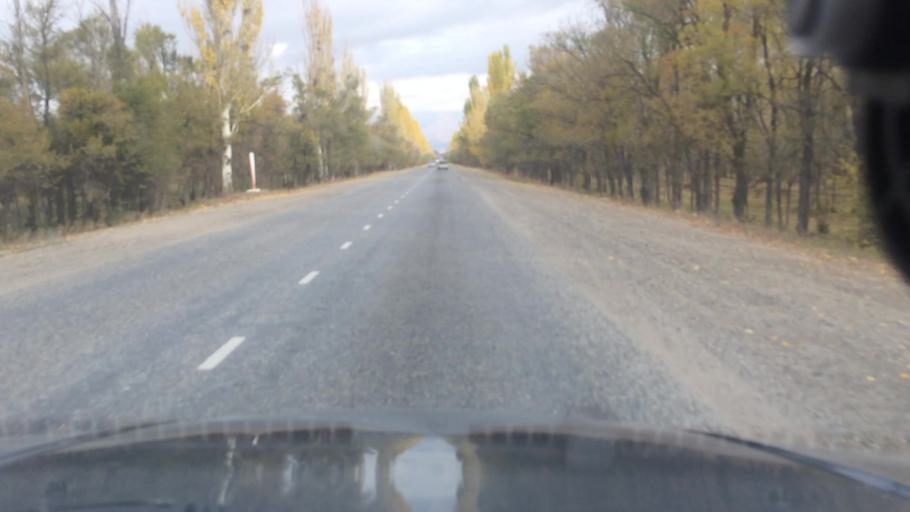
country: KG
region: Ysyk-Koel
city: Tyup
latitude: 42.6331
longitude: 78.3598
